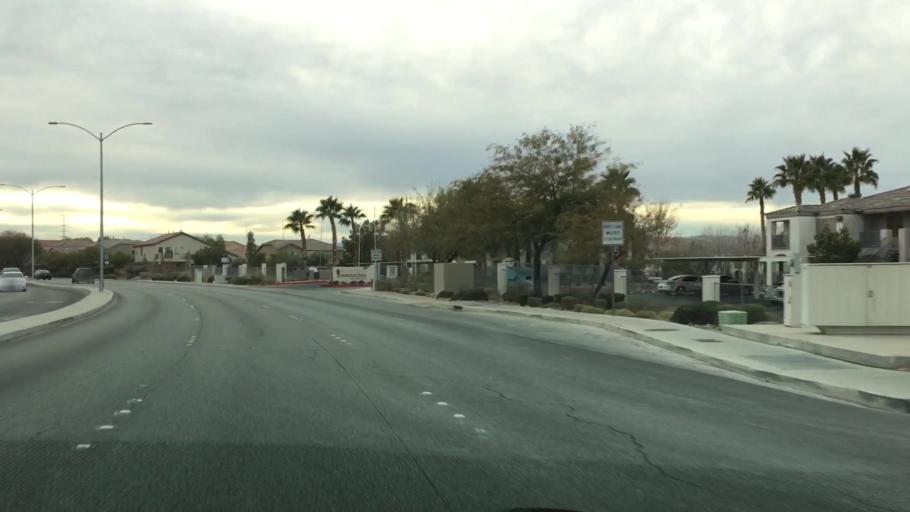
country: US
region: Nevada
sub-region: Clark County
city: Whitney
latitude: 36.0059
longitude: -115.0978
